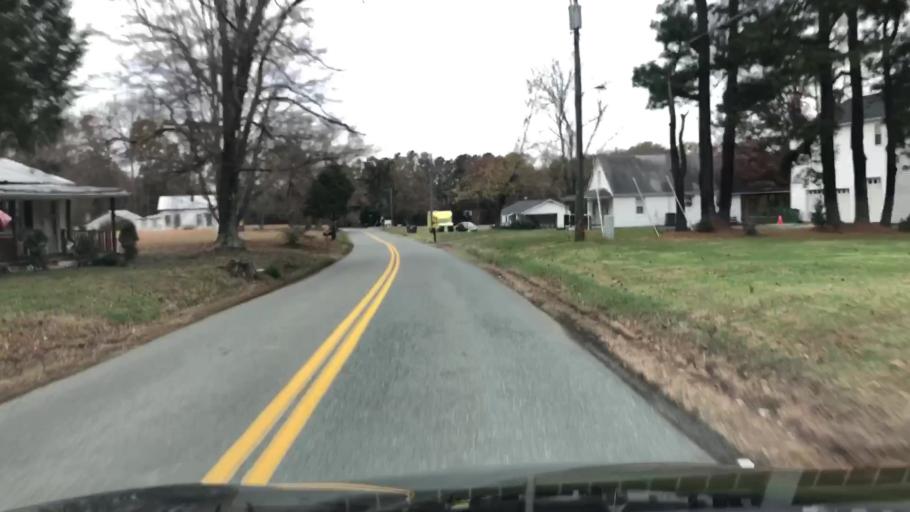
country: US
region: Virginia
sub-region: Stafford County
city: Falmouth
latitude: 38.3957
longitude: -77.5808
